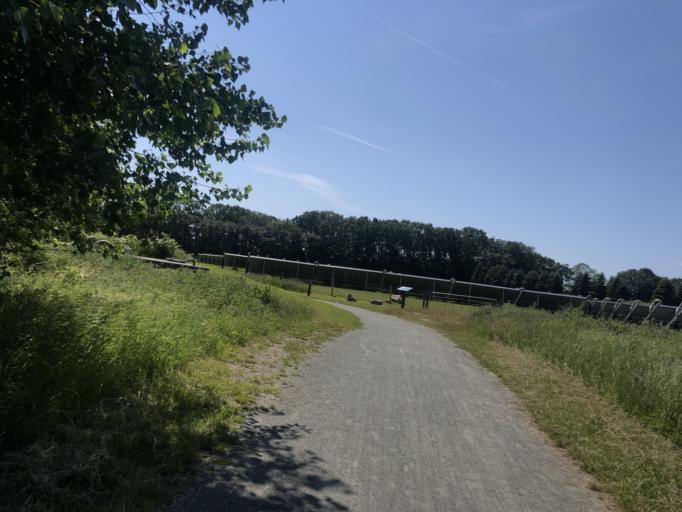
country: DK
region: South Denmark
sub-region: AEro Kommune
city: AEroskobing
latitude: 54.8843
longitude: 10.4160
